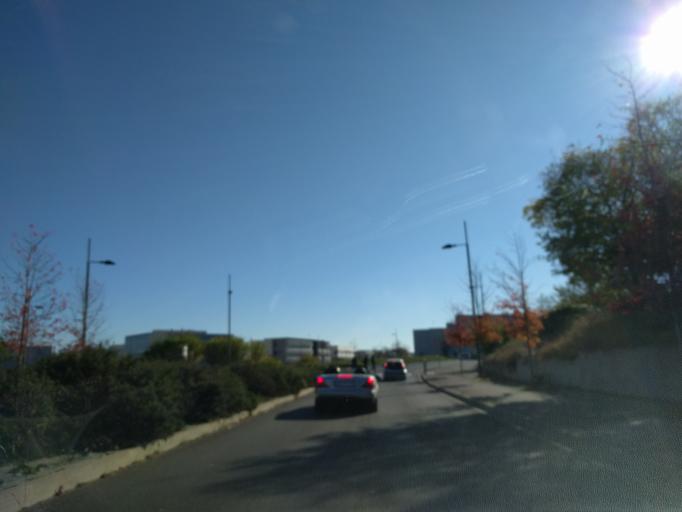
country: FR
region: Languedoc-Roussillon
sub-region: Departement de l'Herault
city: Castelnau-le-Lez
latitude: 43.6193
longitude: 3.9122
